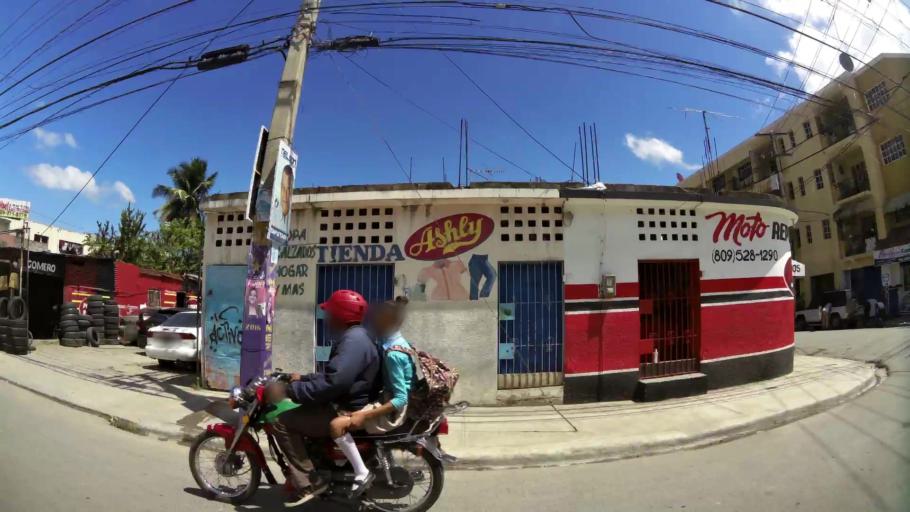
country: DO
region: San Cristobal
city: San Cristobal
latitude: 18.4043
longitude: -70.1065
